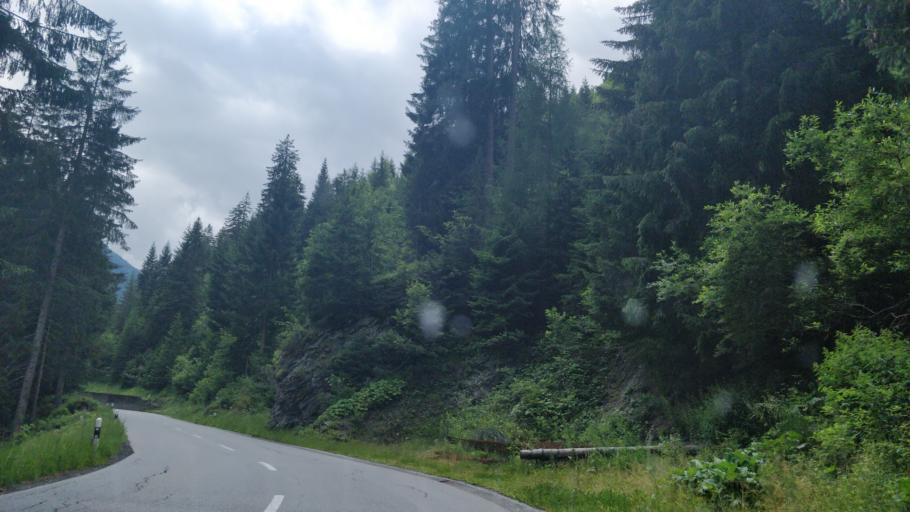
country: CH
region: Grisons
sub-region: Hinterrhein District
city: Hinterrhein
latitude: 46.6410
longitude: 9.1858
